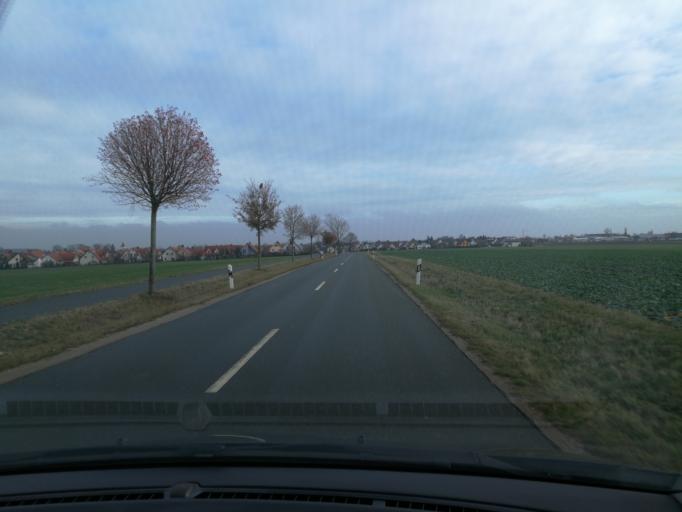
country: DE
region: Bavaria
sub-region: Regierungsbezirk Mittelfranken
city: Obermichelbach
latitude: 49.5288
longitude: 10.8962
